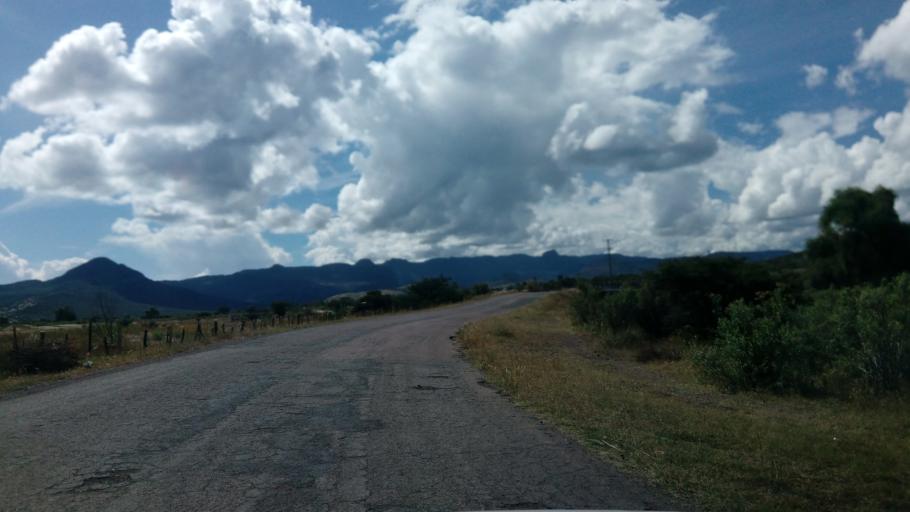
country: MX
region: Durango
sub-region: Durango
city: Jose Refugio Salcido
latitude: 23.7994
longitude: -104.4846
